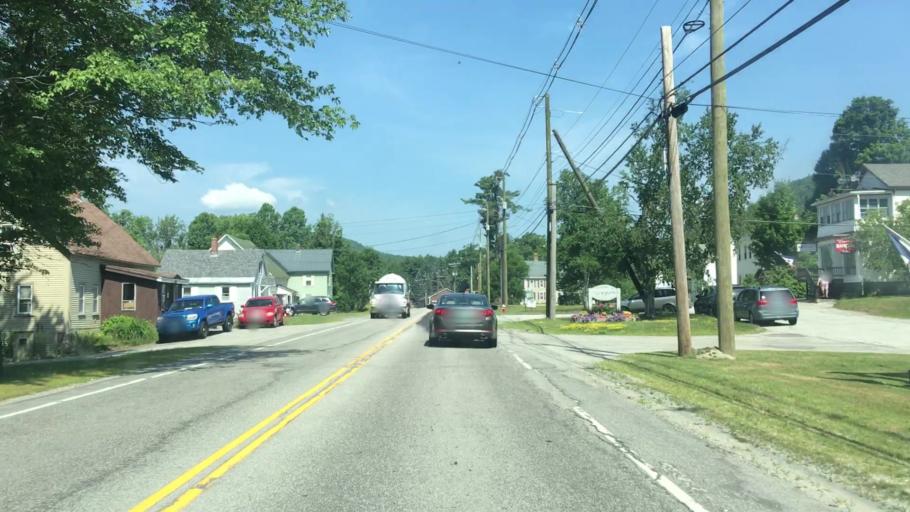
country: US
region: New Hampshire
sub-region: Sullivan County
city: Newport
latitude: 43.3771
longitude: -72.1393
